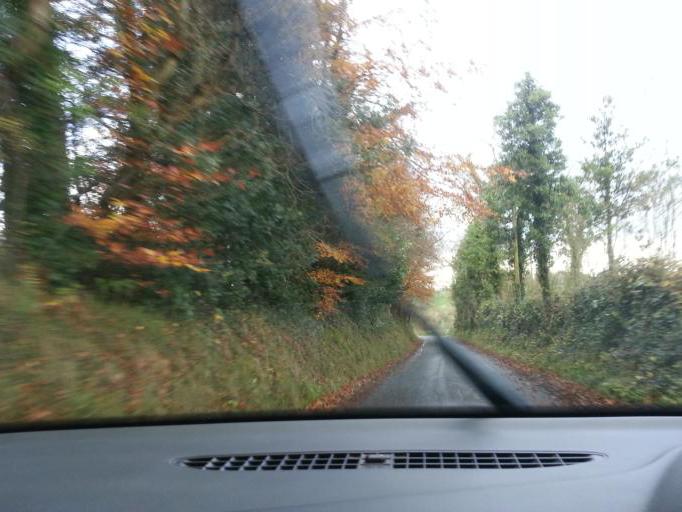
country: IE
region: Ulster
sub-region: County Monaghan
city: Clones
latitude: 54.2295
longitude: -7.2782
